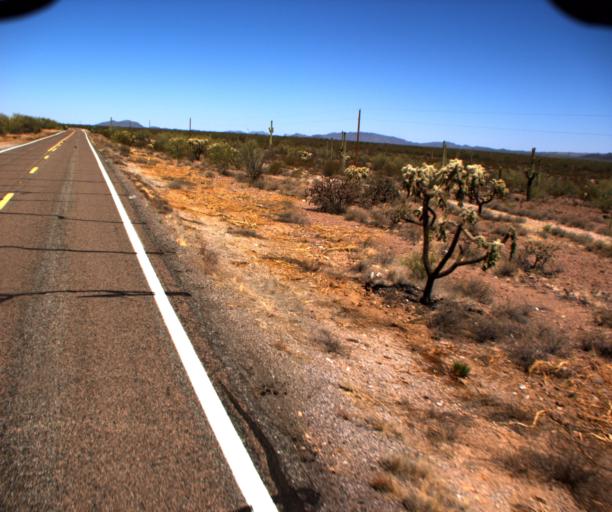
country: US
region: Arizona
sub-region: Pima County
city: Ajo
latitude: 32.2043
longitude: -112.5287
